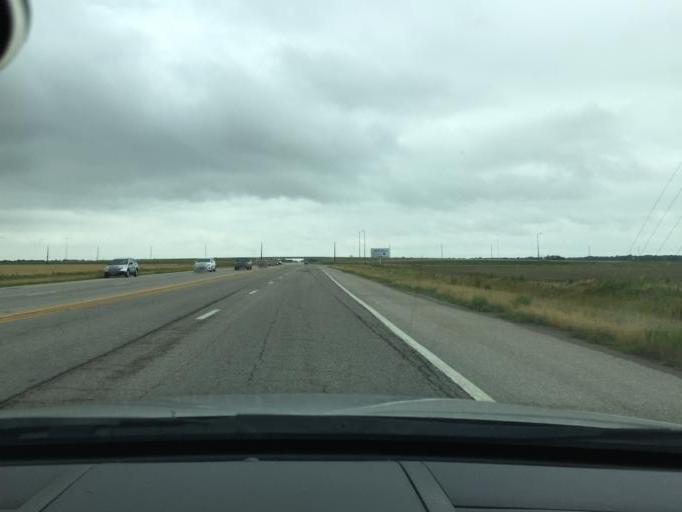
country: US
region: Kansas
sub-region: Reno County
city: Hutchinson
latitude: 38.0360
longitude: -97.8669
